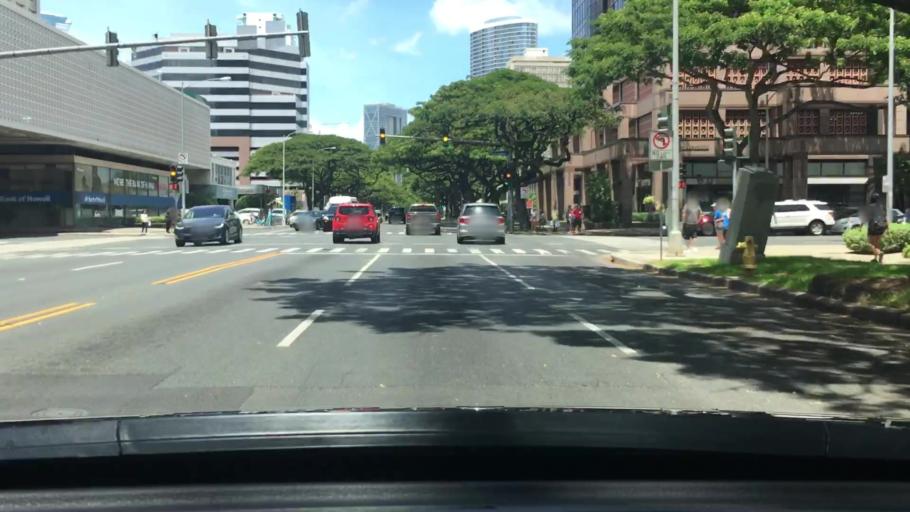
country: US
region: Hawaii
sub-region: Honolulu County
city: Honolulu
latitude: 21.2930
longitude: -157.8421
